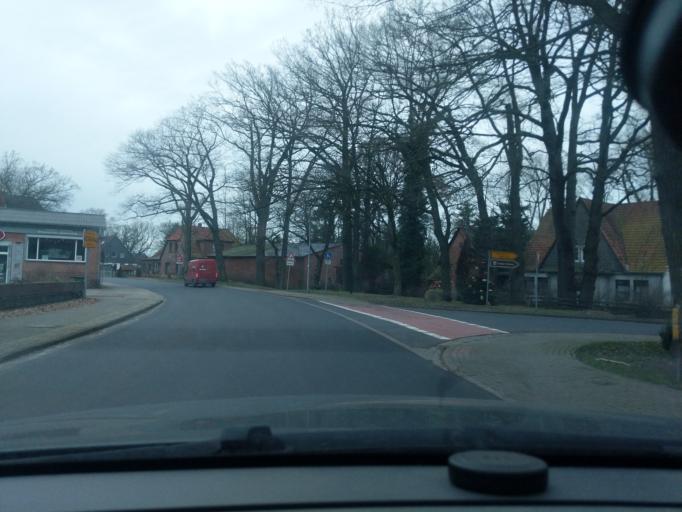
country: DE
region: Lower Saxony
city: Helvesiek
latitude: 53.2157
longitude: 9.4909
